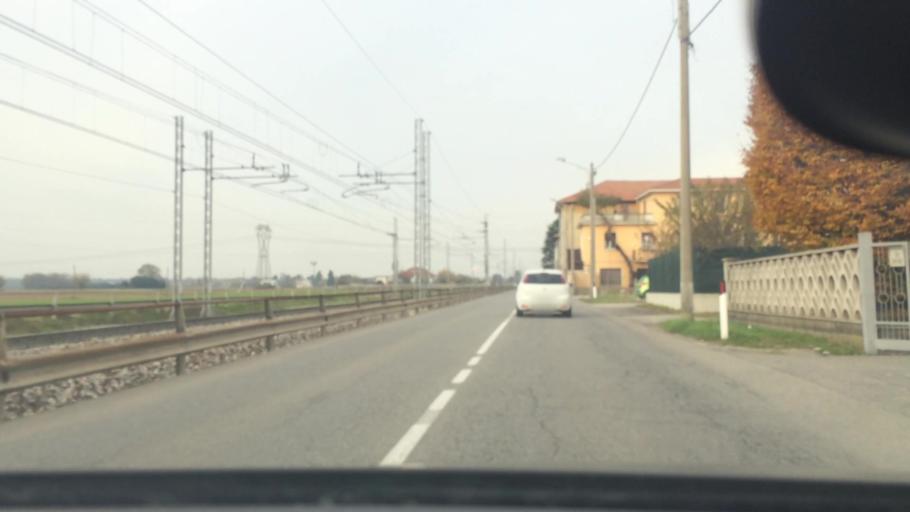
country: IT
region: Lombardy
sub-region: Provincia di Como
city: Rovello Porro
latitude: 45.6561
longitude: 9.0376
